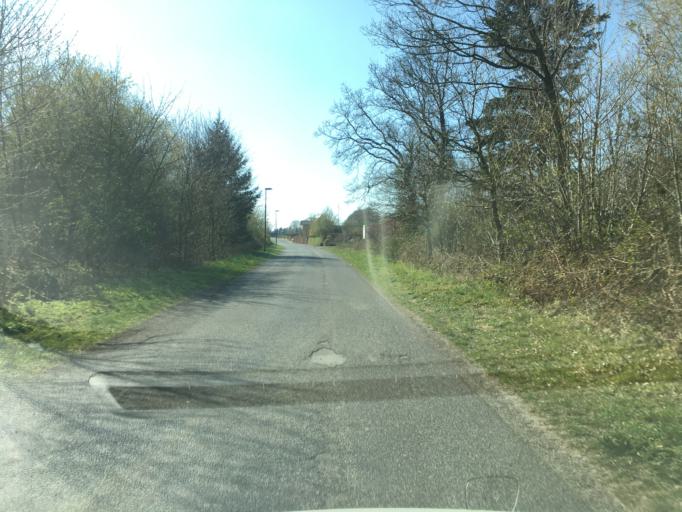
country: DK
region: South Denmark
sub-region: Sonderborg Kommune
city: Grasten
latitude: 54.9281
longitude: 9.4902
